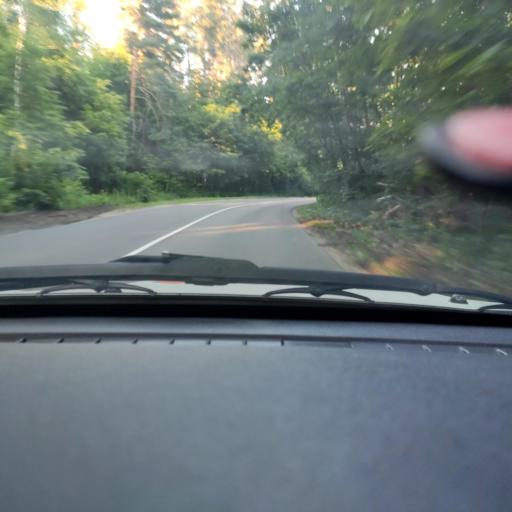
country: RU
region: Voronezj
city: Ramon'
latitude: 51.8934
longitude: 39.2266
